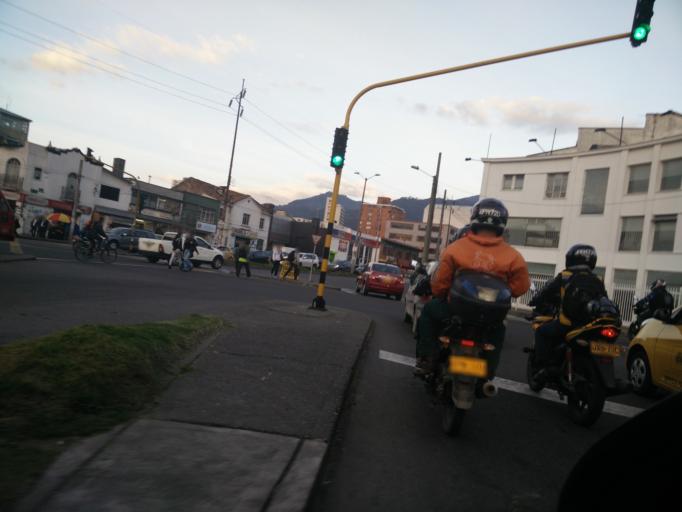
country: CO
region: Bogota D.C.
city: Bogota
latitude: 4.6499
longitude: -74.0678
